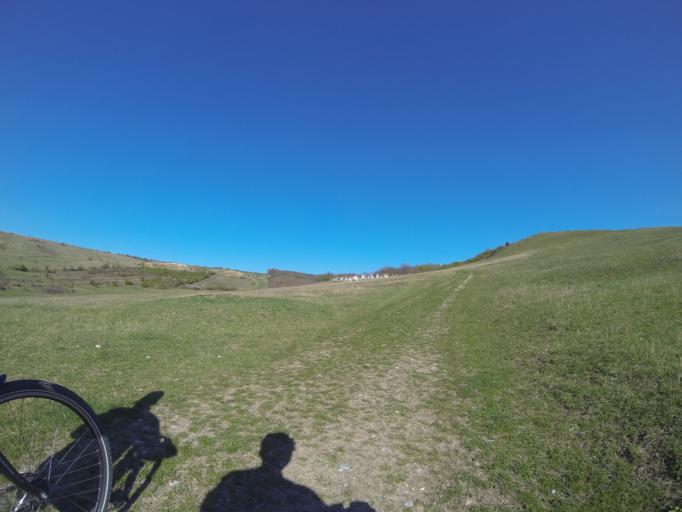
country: RO
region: Dolj
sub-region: Comuna Lipovu
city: Lipovu
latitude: 44.1249
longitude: 23.6301
